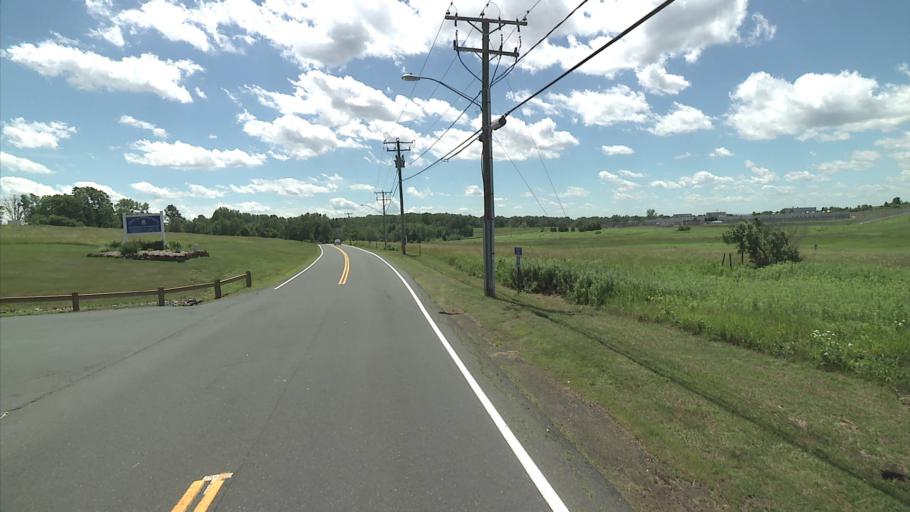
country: US
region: Massachusetts
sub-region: Hampden County
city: East Longmeadow
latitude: 42.0205
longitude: -72.5026
